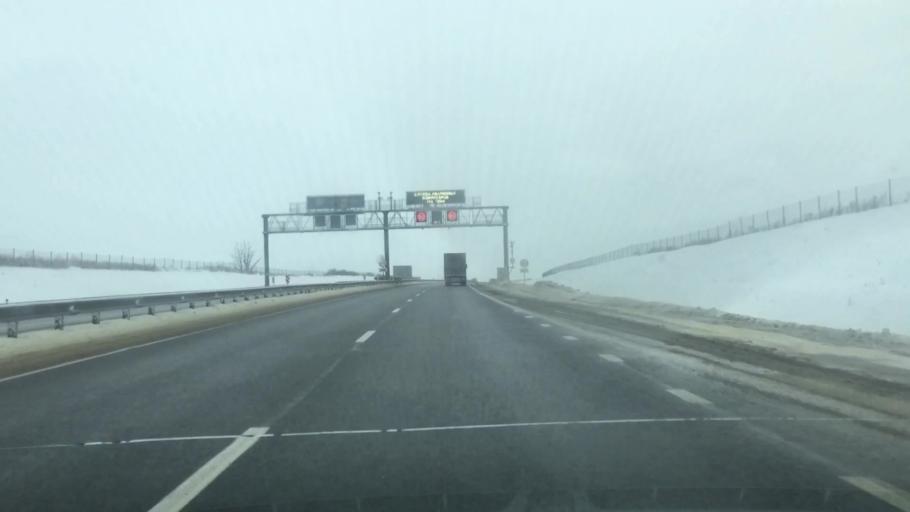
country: RU
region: Tula
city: Yefremov
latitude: 53.1553
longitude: 38.2502
